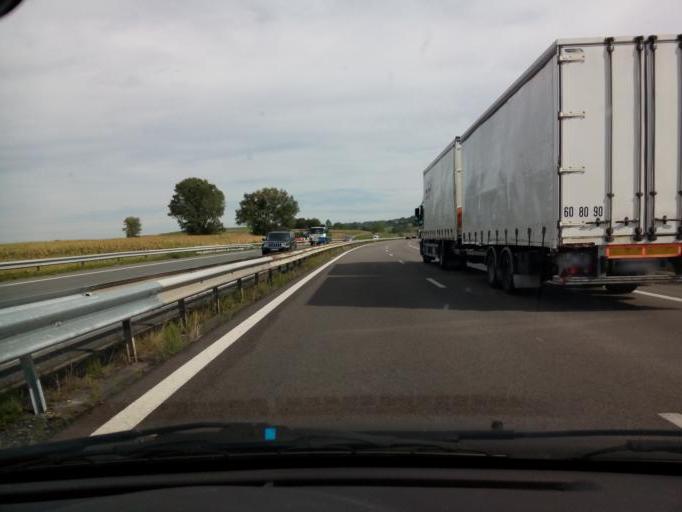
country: FR
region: Rhone-Alpes
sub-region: Departement de l'Isere
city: Cessieu
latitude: 45.5541
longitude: 5.3591
